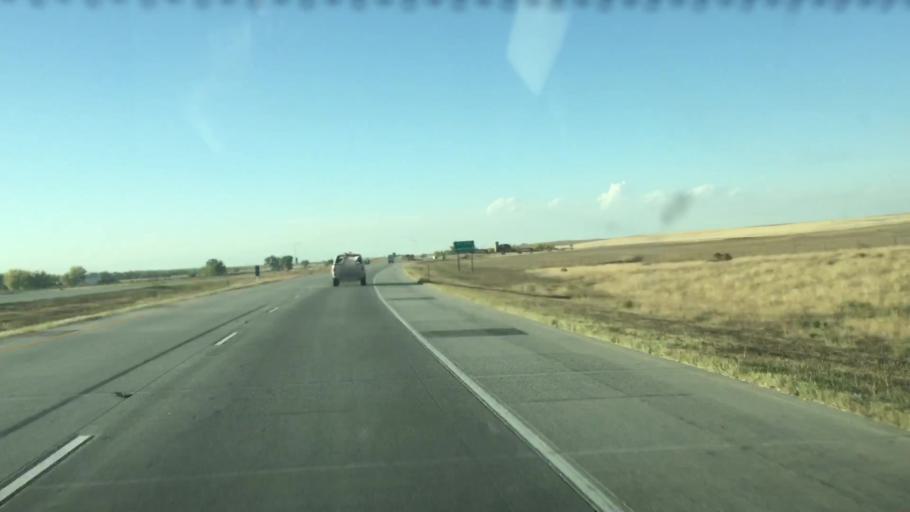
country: US
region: Colorado
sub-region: Arapahoe County
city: Byers
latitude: 39.4992
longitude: -103.9672
